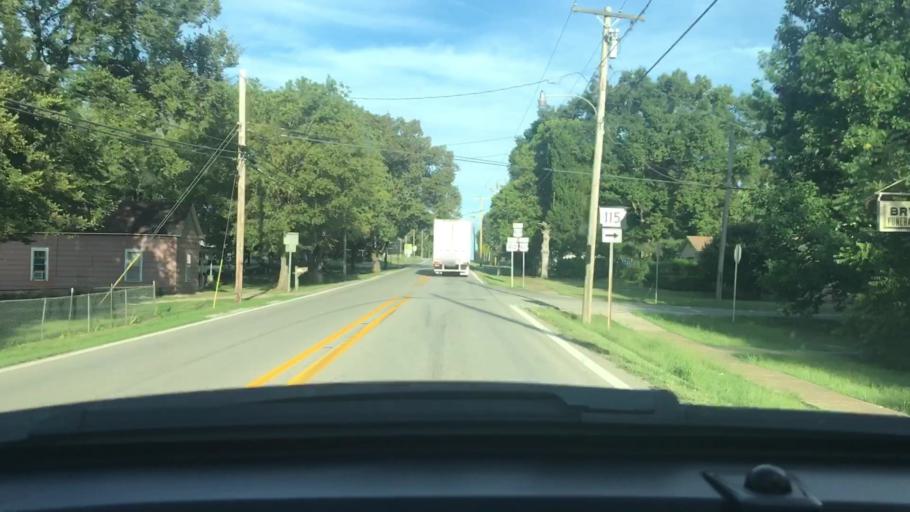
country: US
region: Arkansas
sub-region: Randolph County
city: Pocahontas
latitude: 36.2039
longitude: -91.1840
